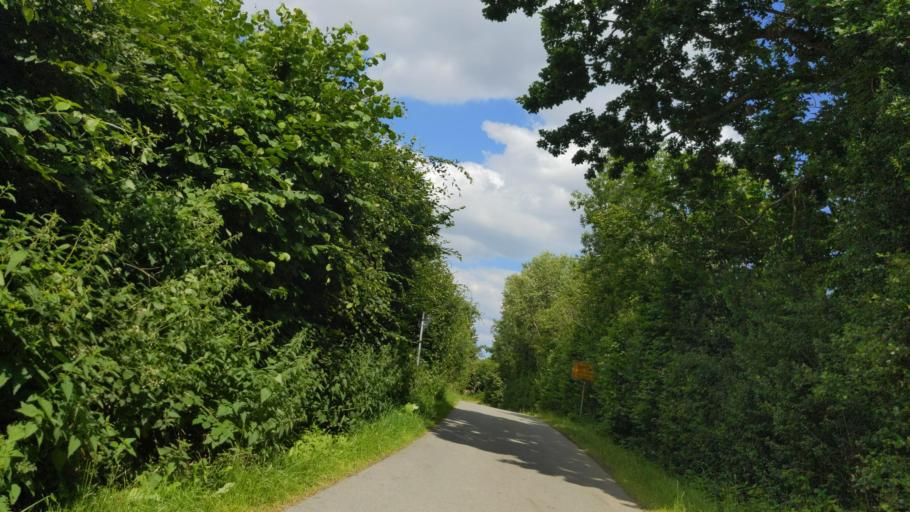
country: DE
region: Schleswig-Holstein
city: Schashagen
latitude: 54.1597
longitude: 10.8839
